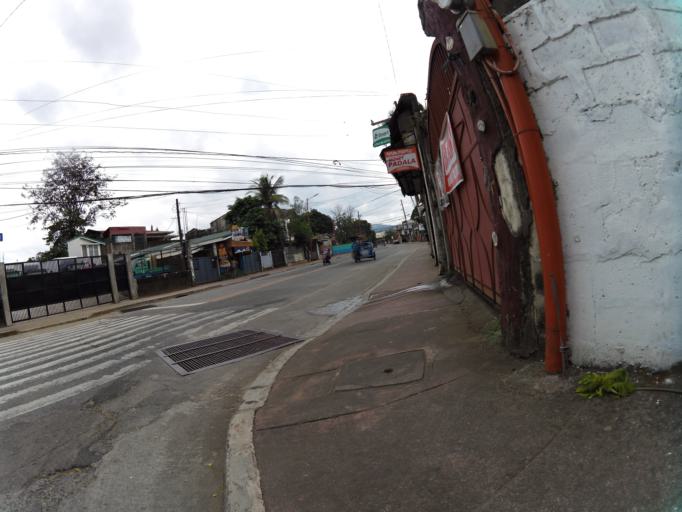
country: PH
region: Calabarzon
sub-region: Province of Rizal
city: Antipolo
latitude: 14.6383
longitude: 121.1131
